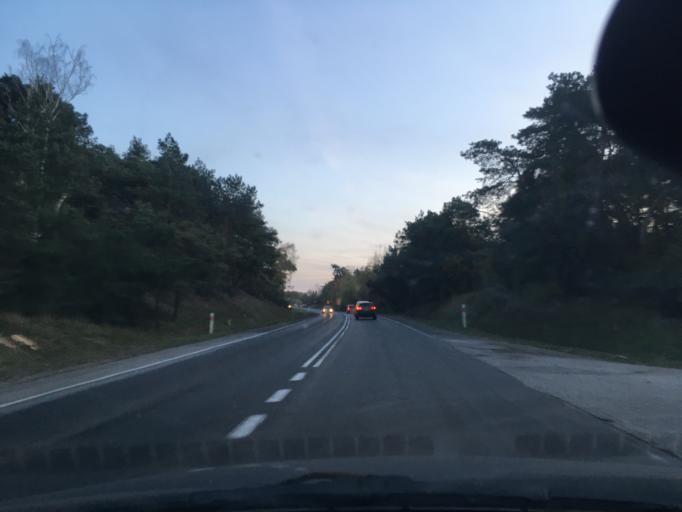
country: PL
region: Masovian Voivodeship
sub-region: Powiat plocki
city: Wyszogrod
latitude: 52.3482
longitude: 20.2100
